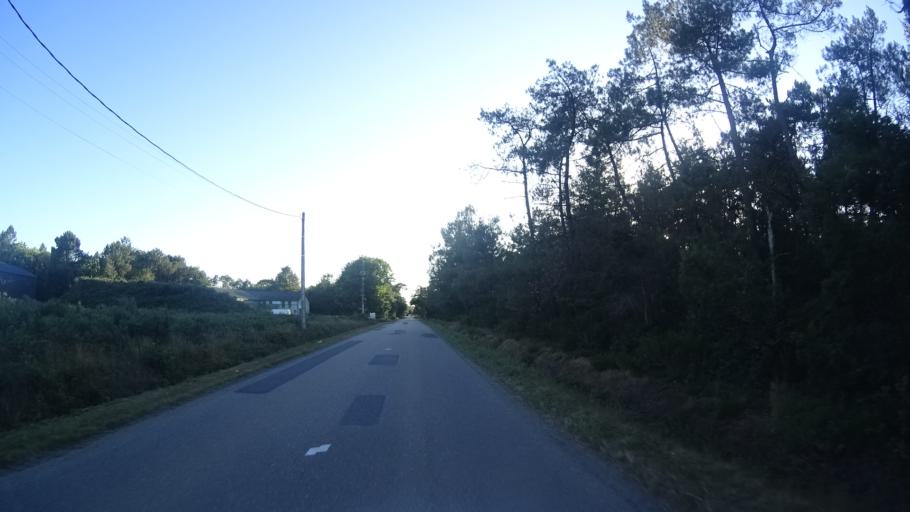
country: FR
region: Brittany
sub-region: Departement d'Ille-et-Vilaine
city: Langon
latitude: 47.7189
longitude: -1.8657
